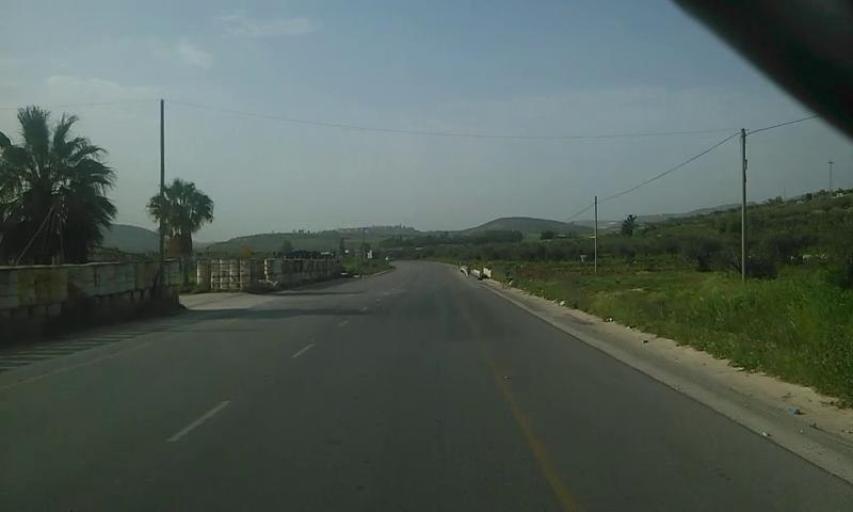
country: PS
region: West Bank
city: Dayr Sharaf
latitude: 32.2624
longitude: 35.1732
